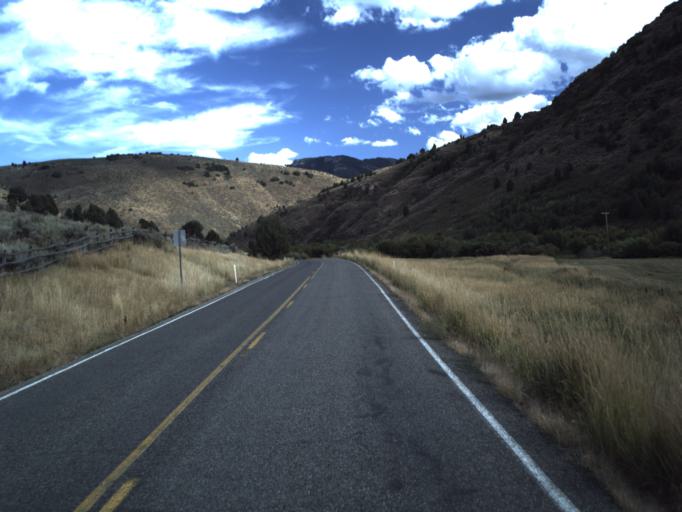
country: US
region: Utah
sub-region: Cache County
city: Millville
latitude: 41.6056
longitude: -111.5794
